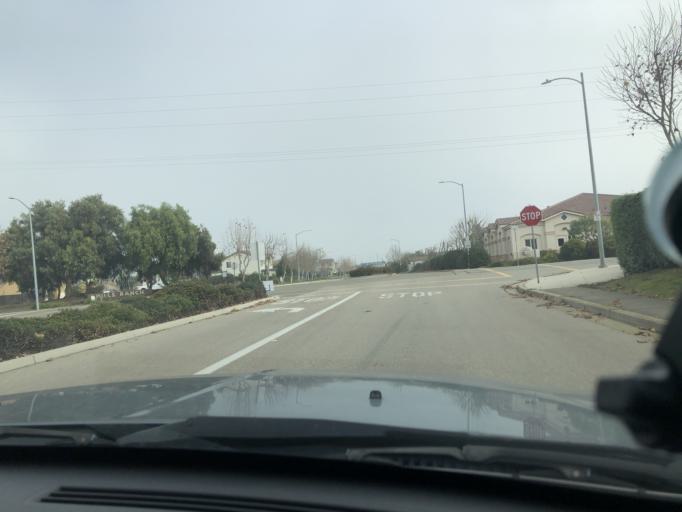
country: US
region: California
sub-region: Monterey County
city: King City
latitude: 36.2194
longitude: -121.1321
